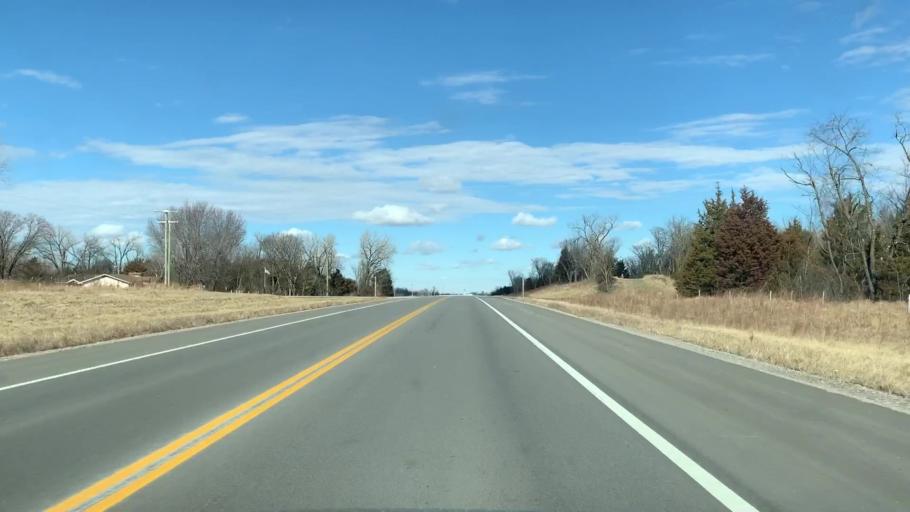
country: US
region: Kansas
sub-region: Crawford County
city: Pittsburg
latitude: 37.3241
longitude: -94.8322
